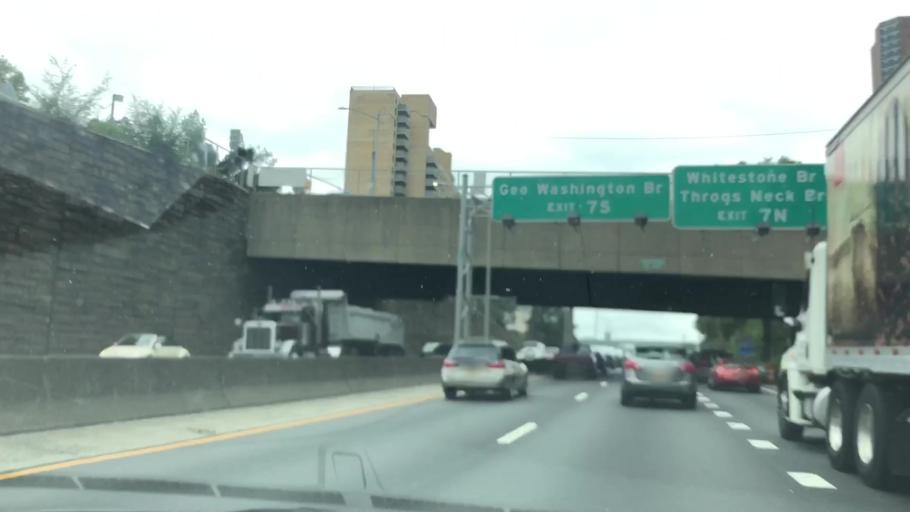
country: US
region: New York
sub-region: New York County
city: Inwood
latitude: 40.8528
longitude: -73.9207
